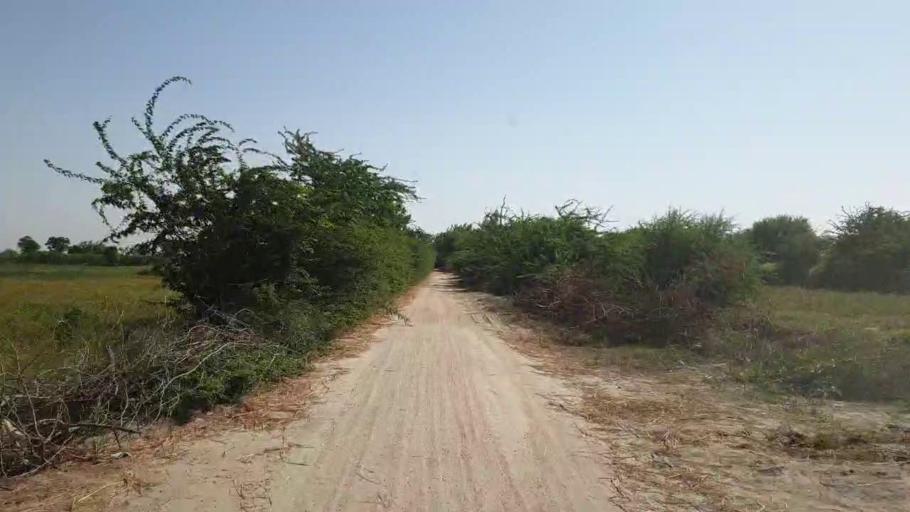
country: PK
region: Sindh
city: Tando Bago
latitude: 24.6500
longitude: 68.9840
